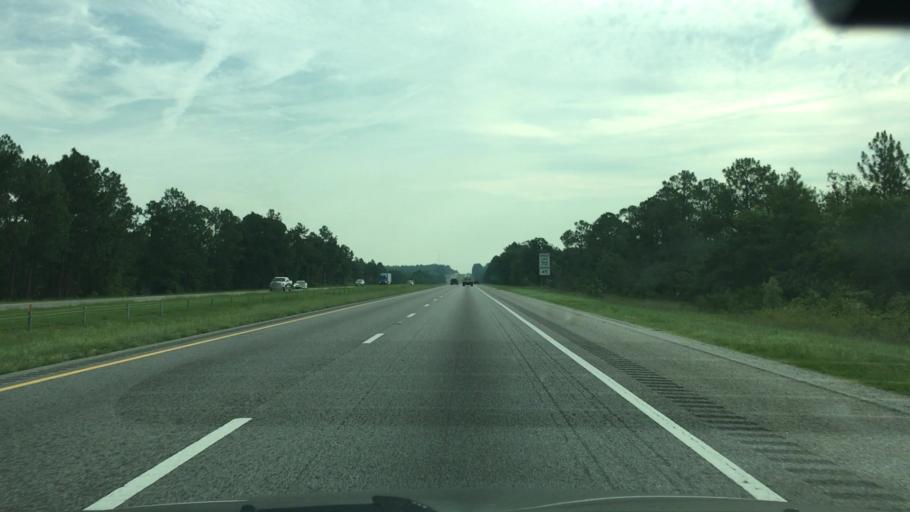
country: US
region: South Carolina
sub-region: Lexington County
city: Batesburg
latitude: 33.7287
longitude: -81.5588
